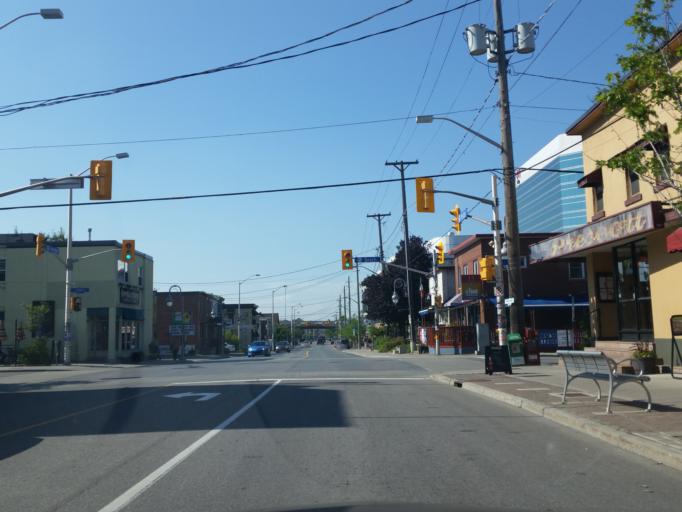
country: CA
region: Ontario
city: Ottawa
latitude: 45.4004
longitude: -75.7093
